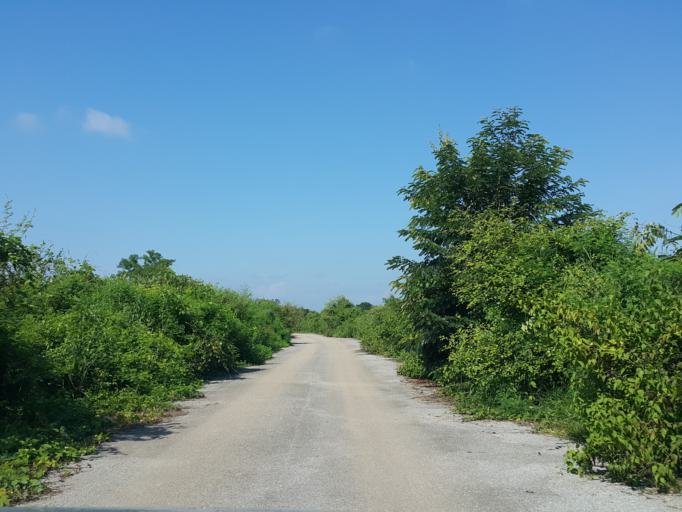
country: TH
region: Chiang Mai
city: Mae On
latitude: 18.8063
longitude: 99.1911
